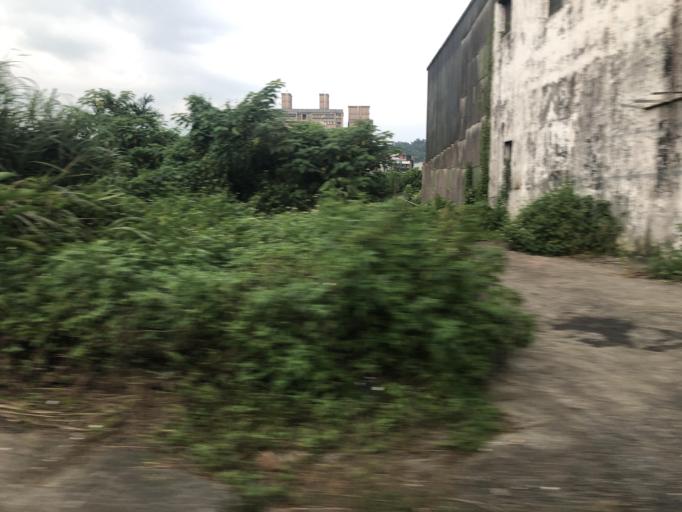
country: TW
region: Taiwan
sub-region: Taoyuan
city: Taoyuan
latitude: 24.9212
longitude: 121.3639
